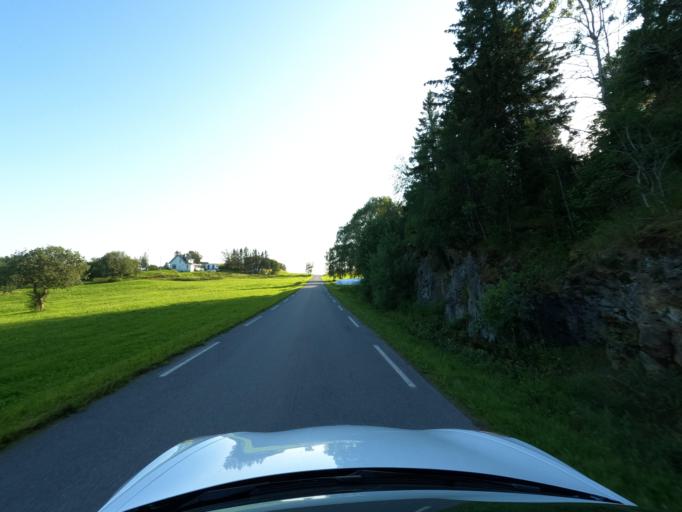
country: NO
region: Nordland
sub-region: Evenes
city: Randa
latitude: 68.4725
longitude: 16.8745
